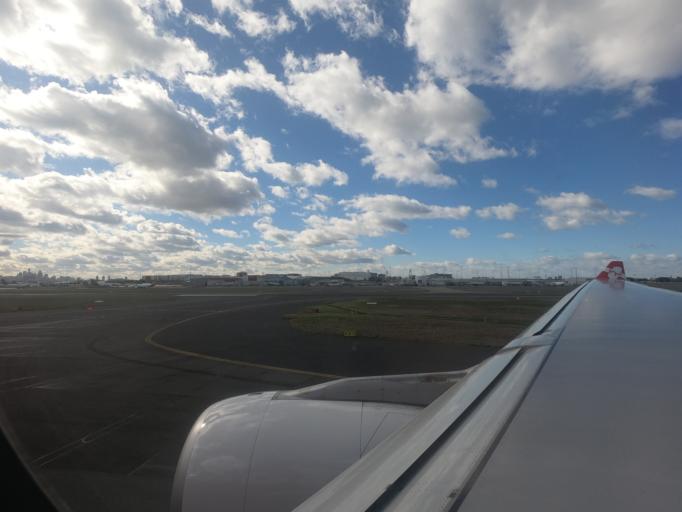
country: AU
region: New South Wales
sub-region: Rockdale
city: Arncliffe
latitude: -33.9351
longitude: 151.1711
